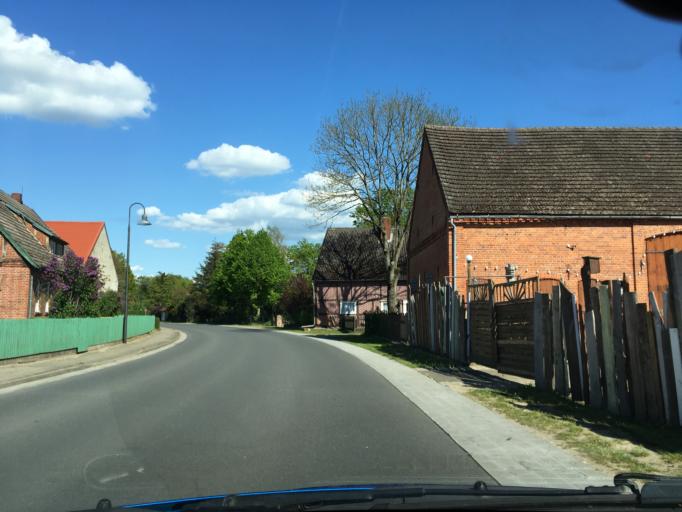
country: DE
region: Lower Saxony
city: Gartow
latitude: 53.0172
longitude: 11.5361
